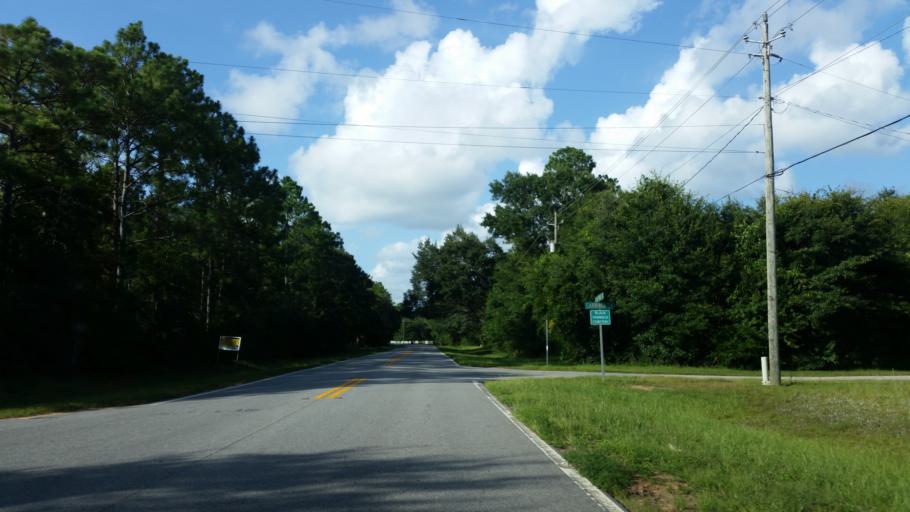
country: US
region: Florida
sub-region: Santa Rosa County
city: Bagdad
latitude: 30.4997
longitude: -87.0610
